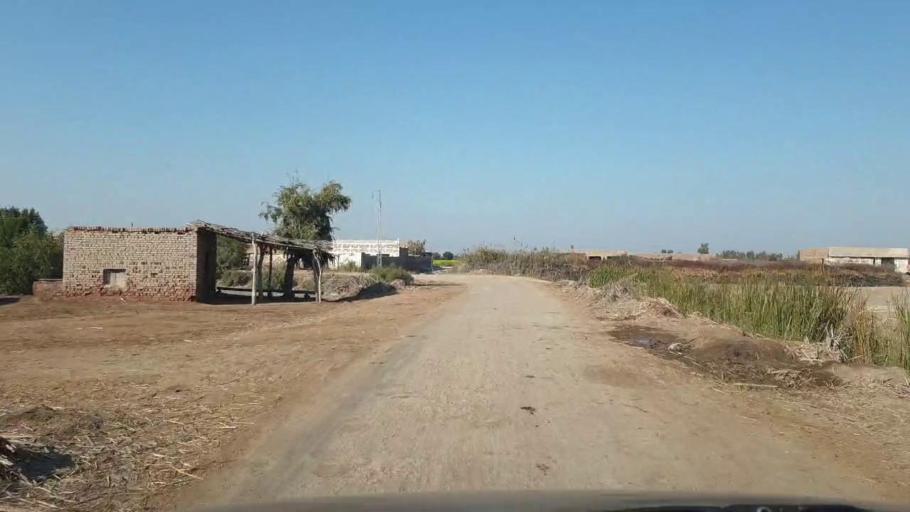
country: PK
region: Sindh
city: Shahpur Chakar
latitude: 26.1718
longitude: 68.6811
